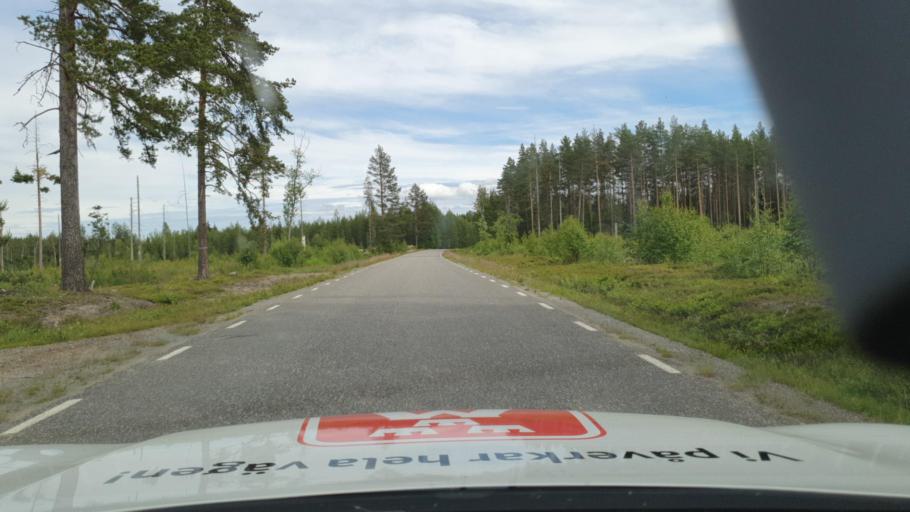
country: SE
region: Vaesterbotten
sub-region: Skelleftea Kommun
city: Viken
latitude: 64.4978
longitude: 20.8940
